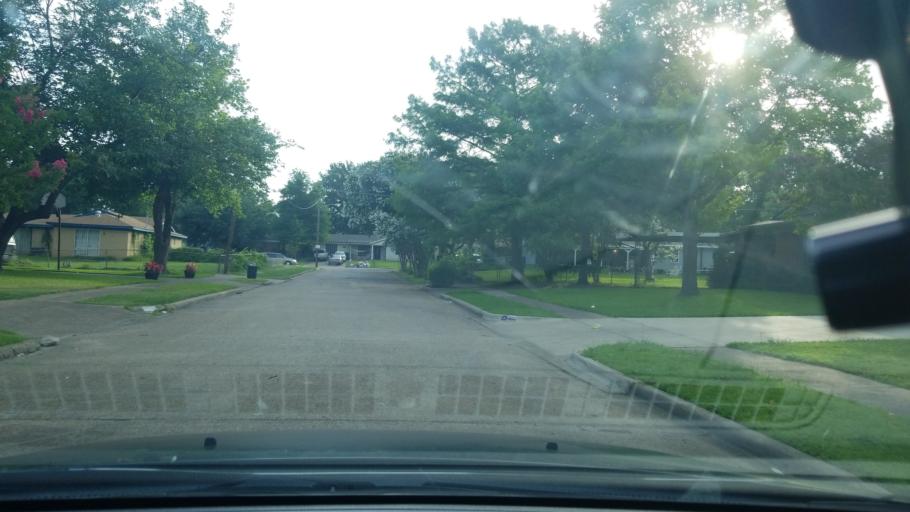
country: US
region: Texas
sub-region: Dallas County
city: Mesquite
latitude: 32.8294
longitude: -96.6493
